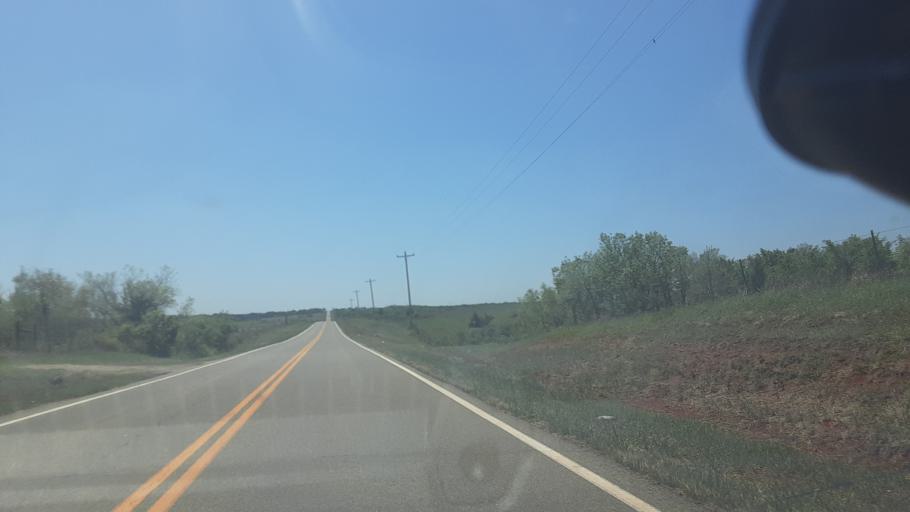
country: US
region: Oklahoma
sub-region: Logan County
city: Guthrie
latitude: 36.0418
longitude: -97.4080
